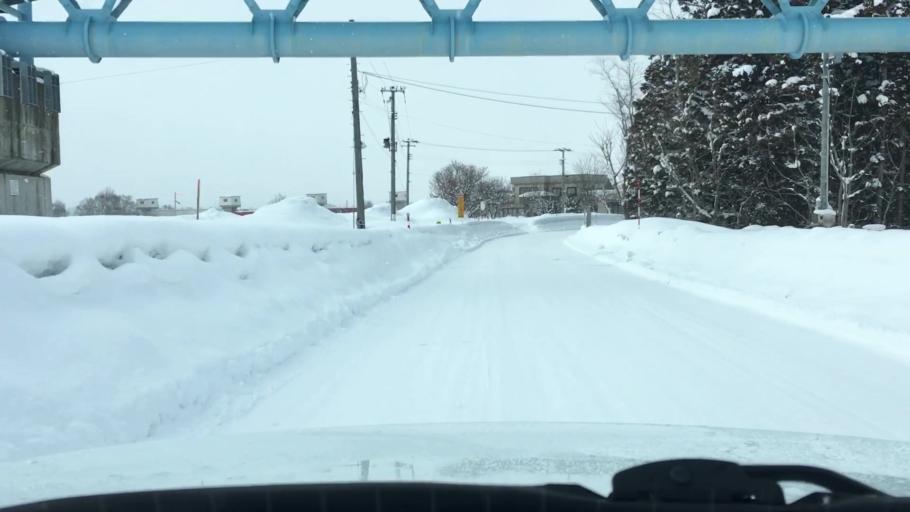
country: JP
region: Aomori
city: Hirosaki
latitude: 40.6524
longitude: 140.4822
